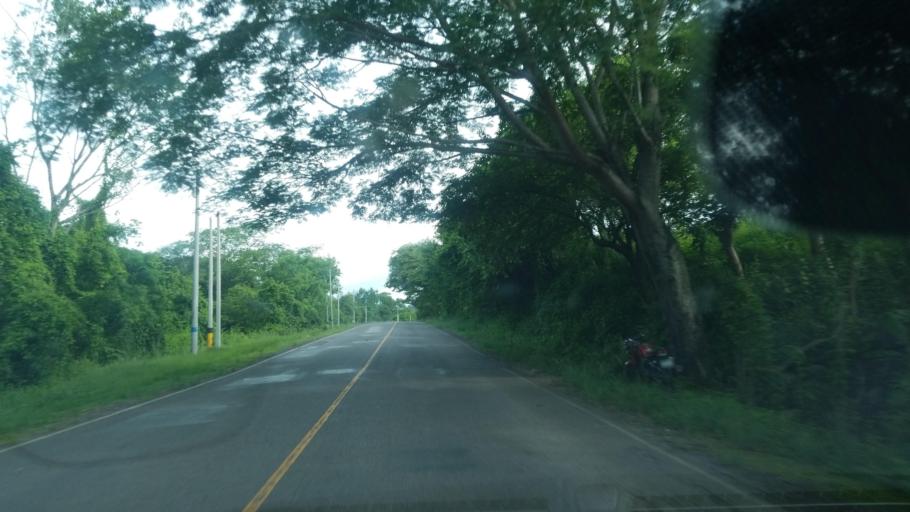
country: HN
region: Santa Barbara
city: Trinidad
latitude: 15.1187
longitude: -88.2010
